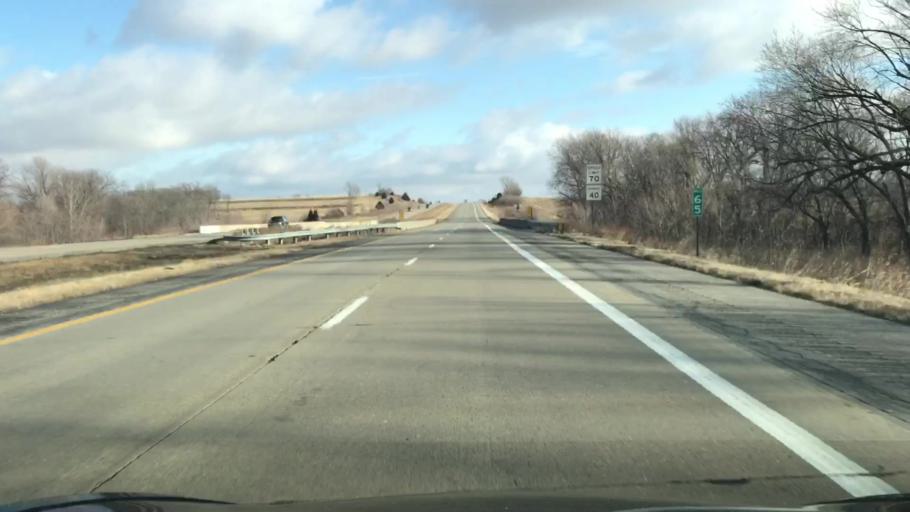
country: US
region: Iowa
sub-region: Cass County
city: Atlantic
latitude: 41.4972
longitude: -94.8605
